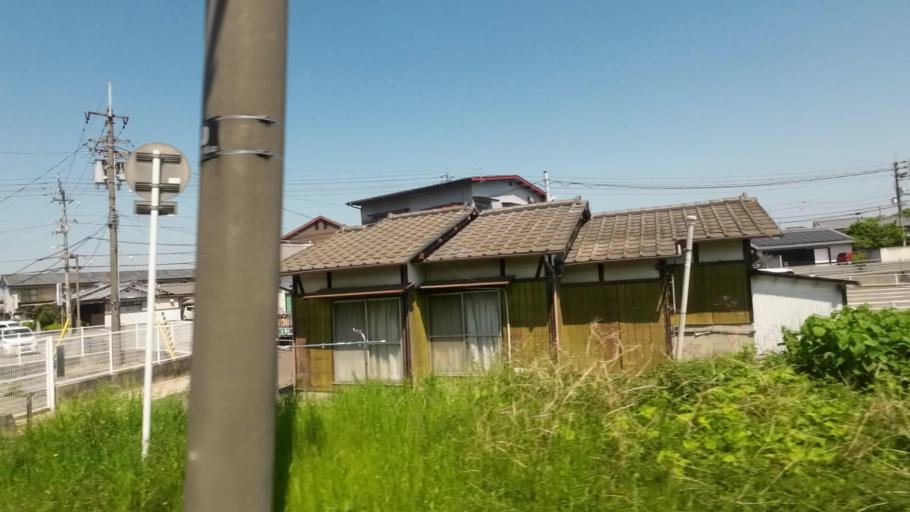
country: JP
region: Ehime
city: Niihama
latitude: 33.9528
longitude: 133.3000
